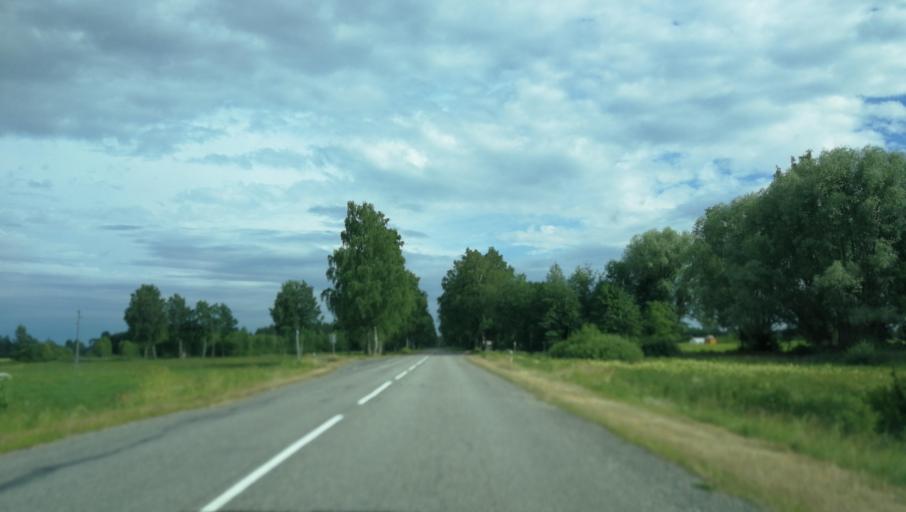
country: LV
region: Valmieras Rajons
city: Valmiera
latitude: 57.6474
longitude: 25.4364
